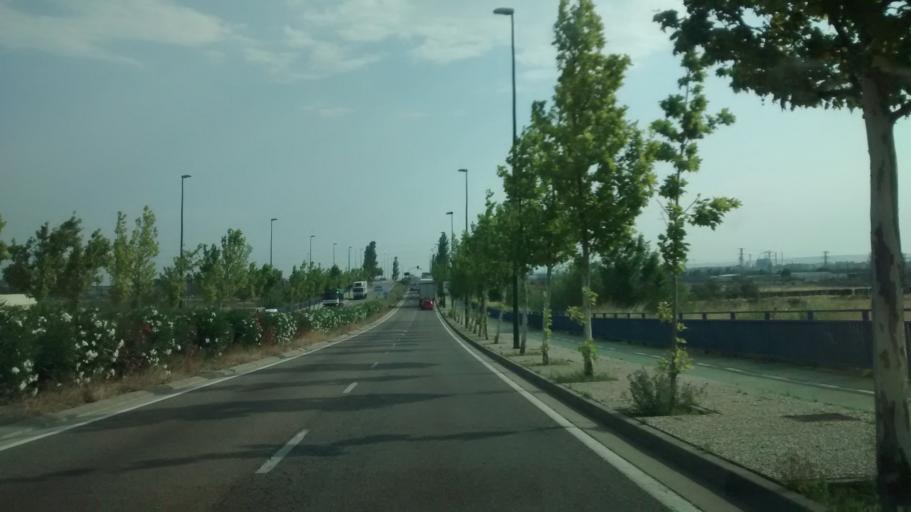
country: ES
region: Aragon
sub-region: Provincia de Zaragoza
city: Zaragoza
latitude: 41.6750
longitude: -0.8536
